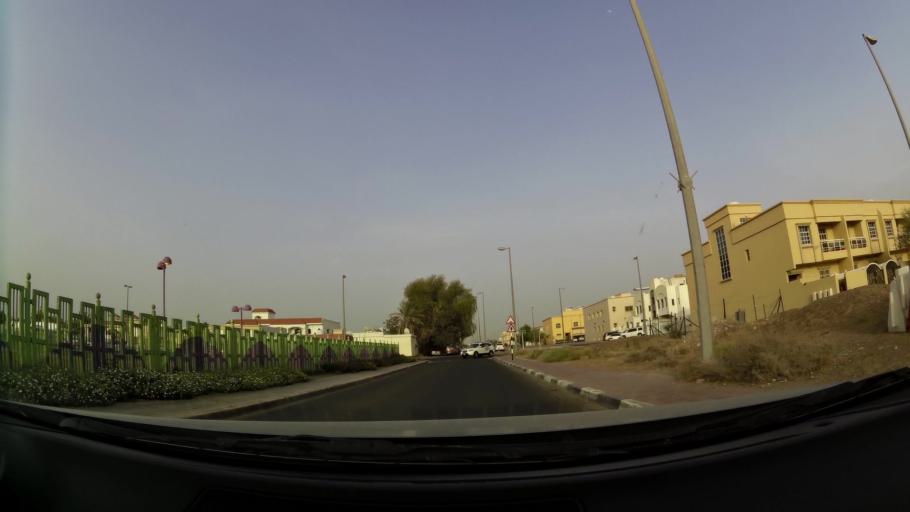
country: OM
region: Al Buraimi
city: Al Buraymi
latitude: 24.2429
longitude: 55.7409
